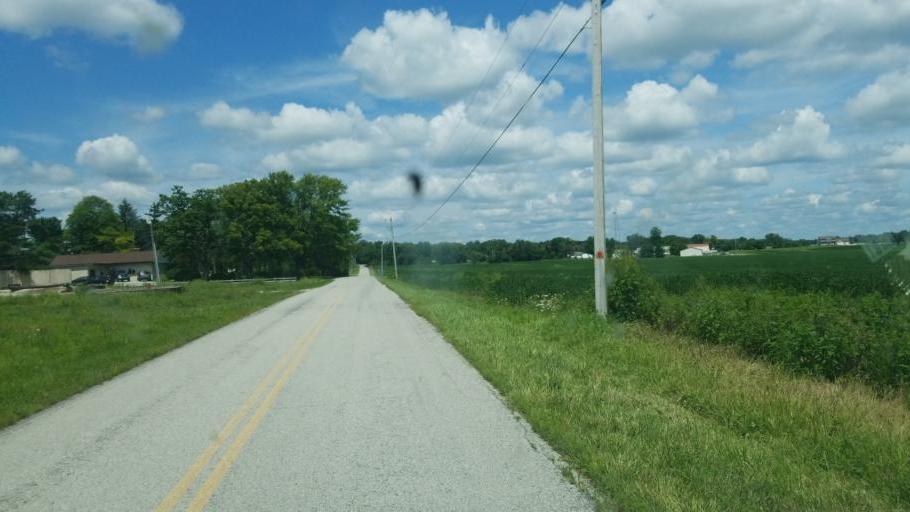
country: US
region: Ohio
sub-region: Delaware County
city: Sunbury
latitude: 40.3129
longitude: -82.8273
